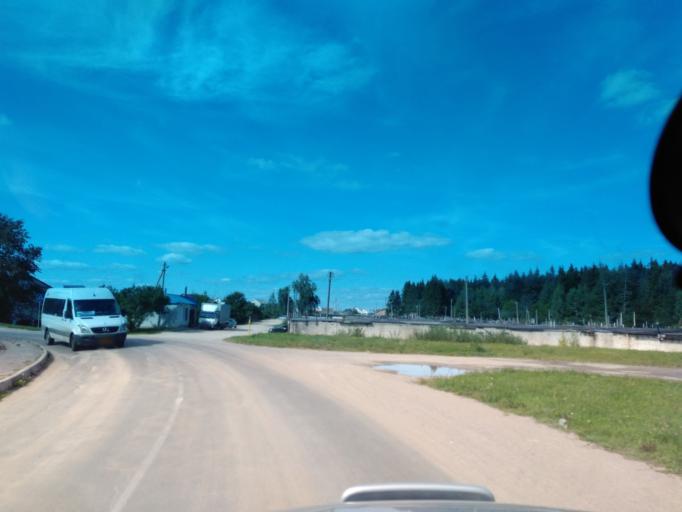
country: BY
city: Fanipol
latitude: 53.7478
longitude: 27.3416
